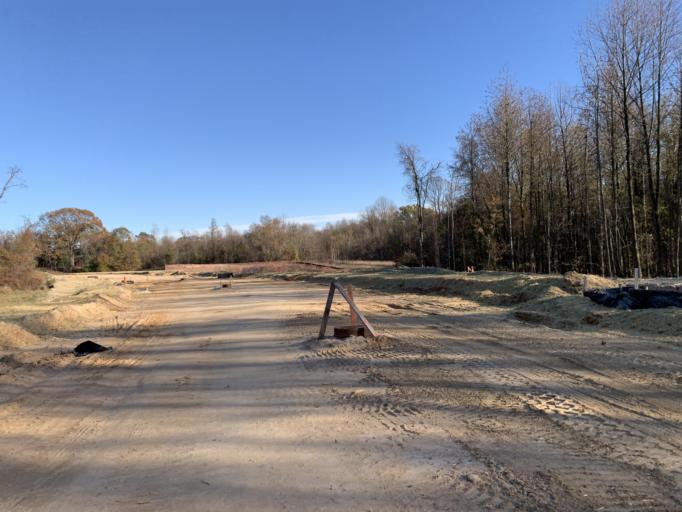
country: US
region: Maryland
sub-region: Baltimore County
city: Middle River
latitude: 39.3513
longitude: -76.4297
